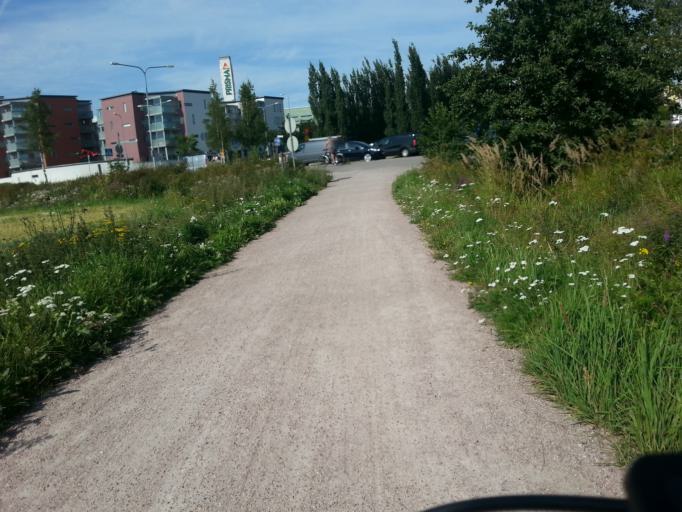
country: FI
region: Uusimaa
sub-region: Helsinki
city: Vantaa
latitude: 60.2252
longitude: 25.0091
